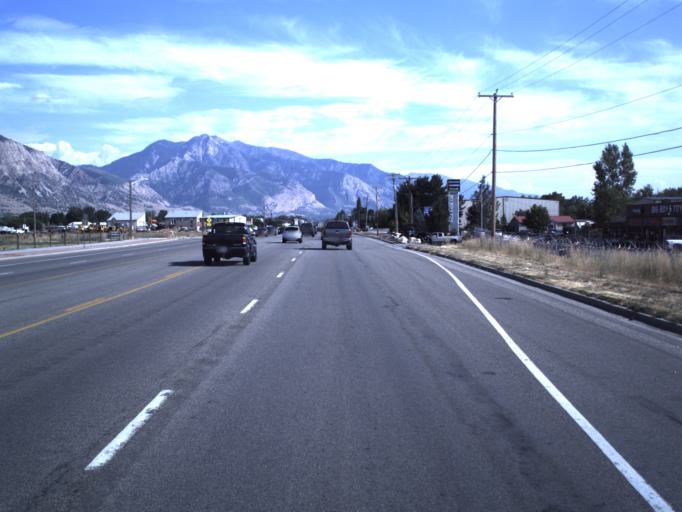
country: US
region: Utah
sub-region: Weber County
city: Pleasant View
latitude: 41.3054
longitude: -112.0044
